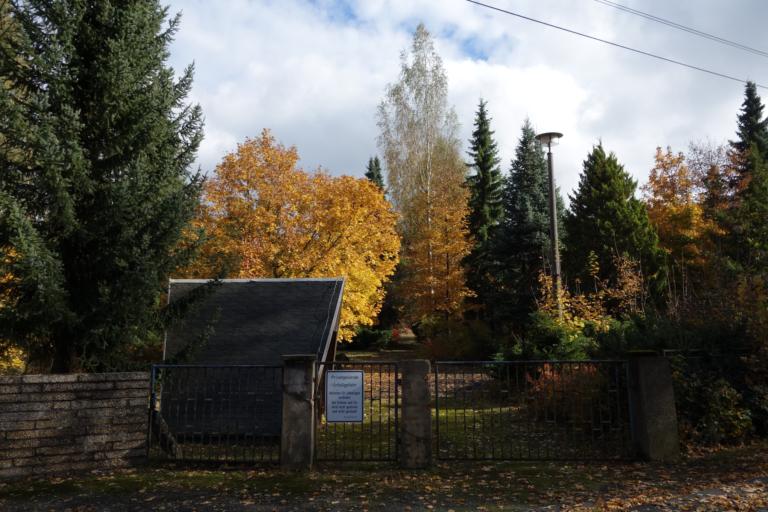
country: DE
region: Saxony
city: Kurort Oybin
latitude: 50.8404
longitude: 14.7476
